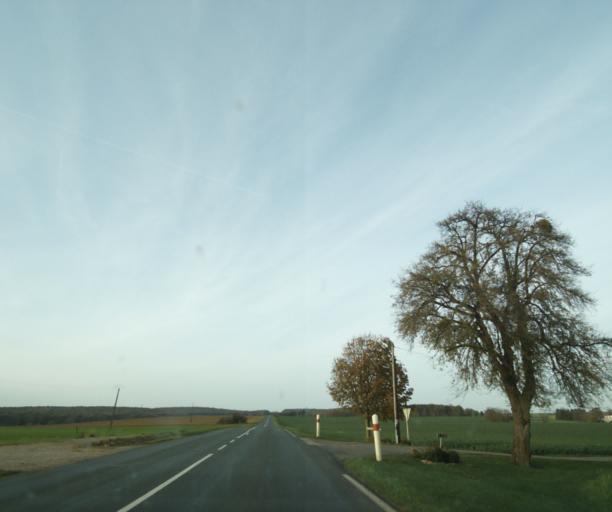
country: FR
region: Lorraine
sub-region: Departement de Meurthe-et-Moselle
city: Longuyon
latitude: 49.3873
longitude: 5.6277
